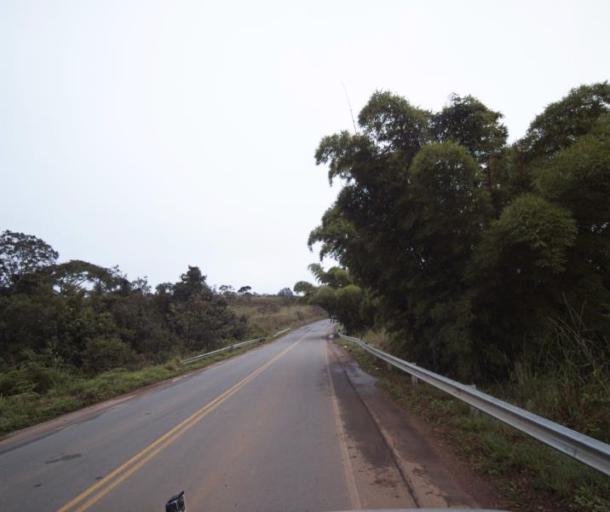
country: BR
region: Goias
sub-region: Pirenopolis
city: Pirenopolis
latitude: -15.8319
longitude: -48.7802
